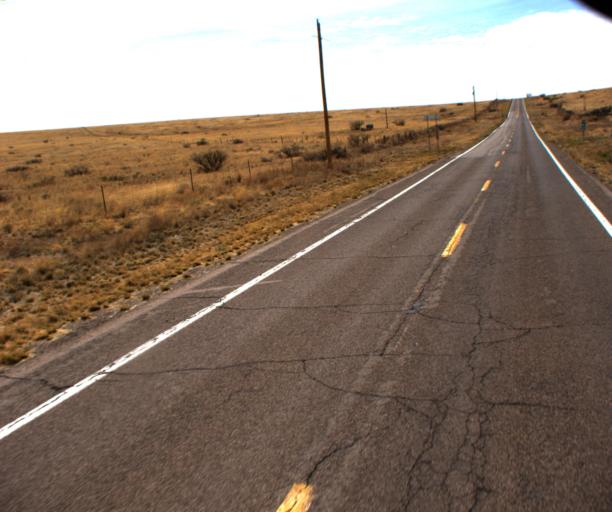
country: US
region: Arizona
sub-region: Cochise County
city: Willcox
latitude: 32.0068
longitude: -109.4225
